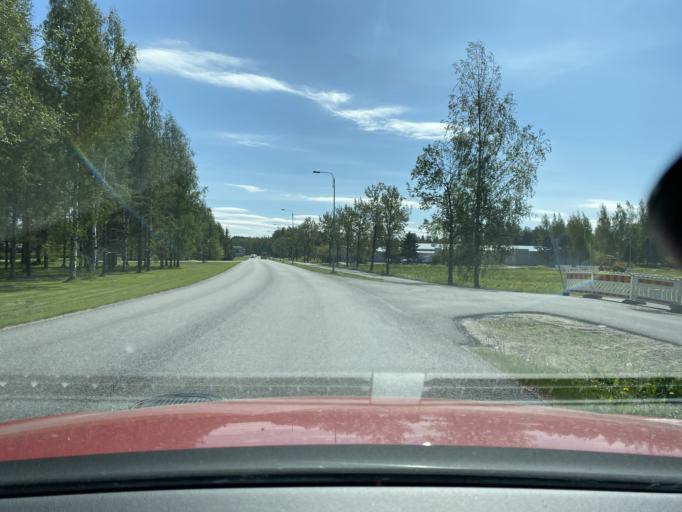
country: FI
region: Satakunta
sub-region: Rauma
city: Eura
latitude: 61.1264
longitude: 22.1472
